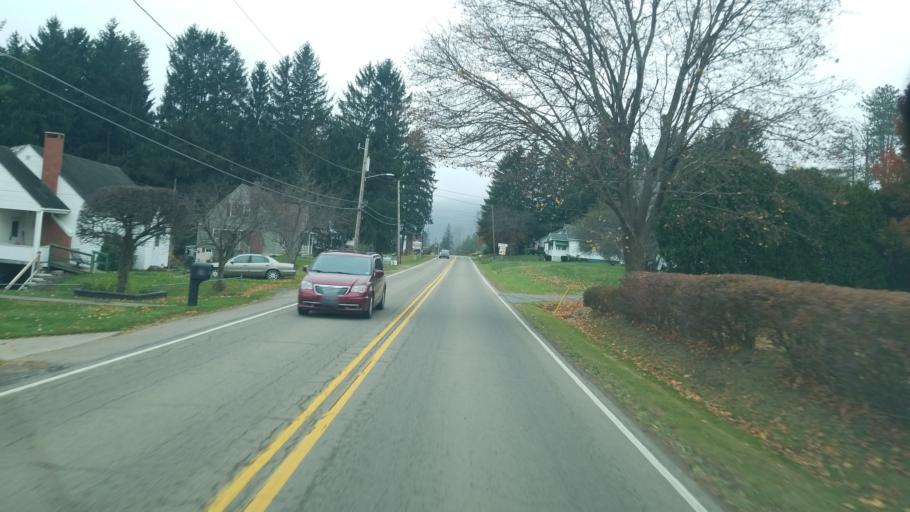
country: US
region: Pennsylvania
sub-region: McKean County
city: Smethport
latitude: 41.8104
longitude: -78.4584
